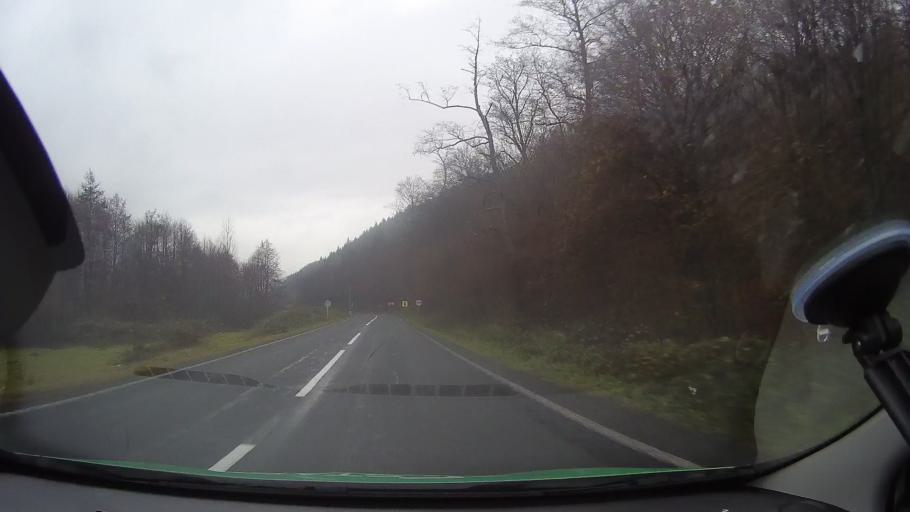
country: RO
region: Arad
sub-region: Comuna Plescuta
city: Plescuta
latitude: 46.3014
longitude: 22.4558
